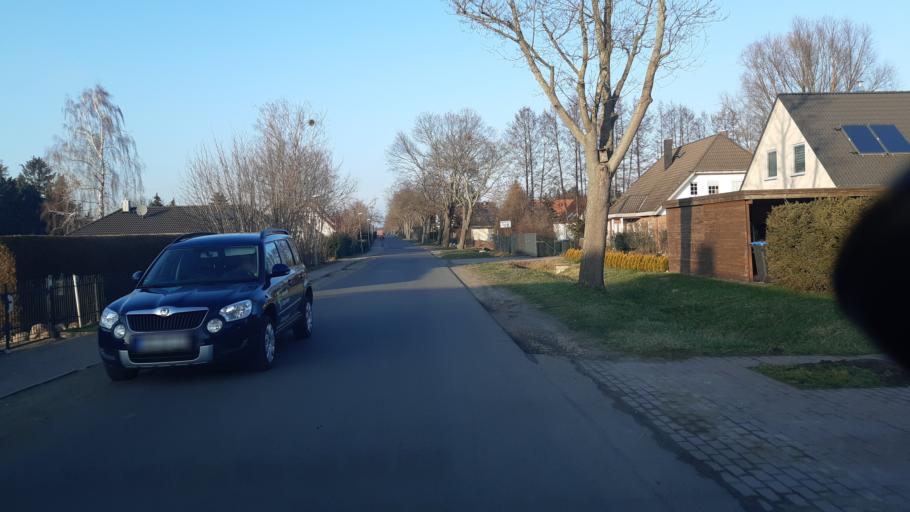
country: DE
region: Brandenburg
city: Velten
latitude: 52.7099
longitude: 13.1484
